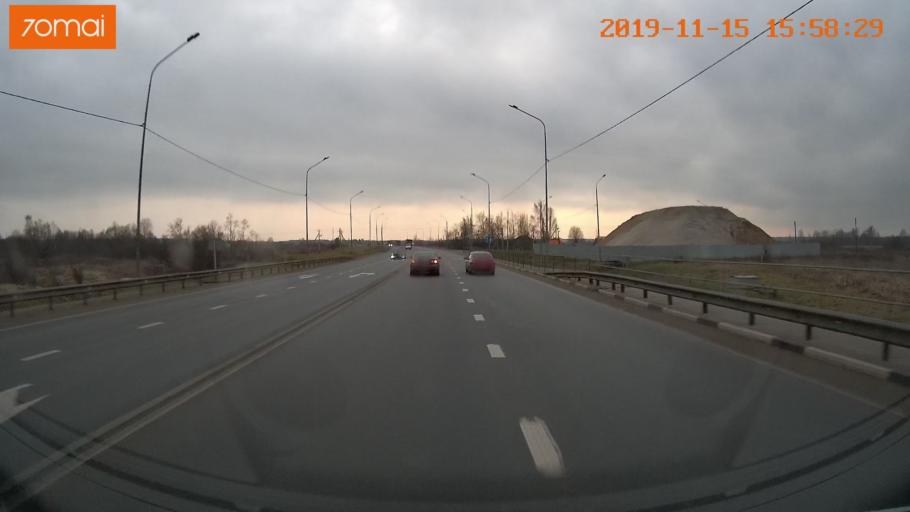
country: RU
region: Jaroslavl
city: Yaroslavl
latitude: 57.8197
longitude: 39.9533
